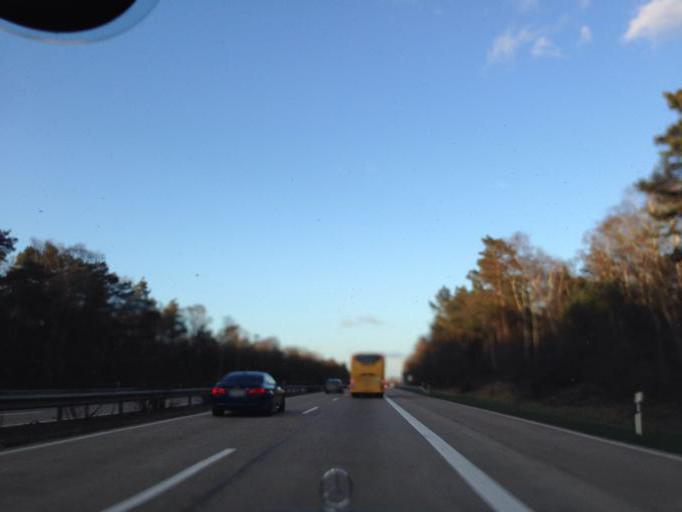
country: DE
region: Lower Saxony
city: Soltau
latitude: 52.9191
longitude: 9.8082
